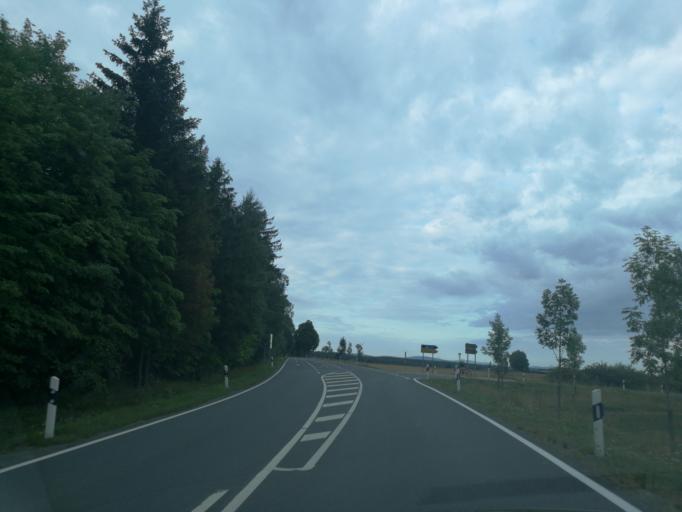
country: DE
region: Saxony
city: Eichigt
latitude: 50.3329
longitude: 12.1592
